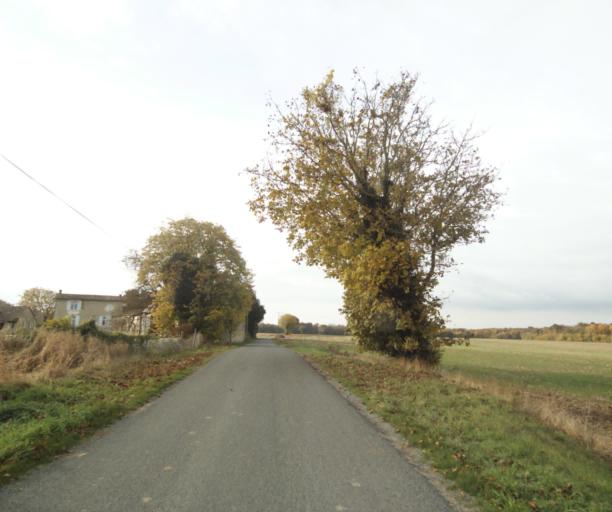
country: FR
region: Poitou-Charentes
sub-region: Departement de la Charente-Maritime
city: Saint-Georges-des-Coteaux
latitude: 45.7743
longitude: -0.7248
